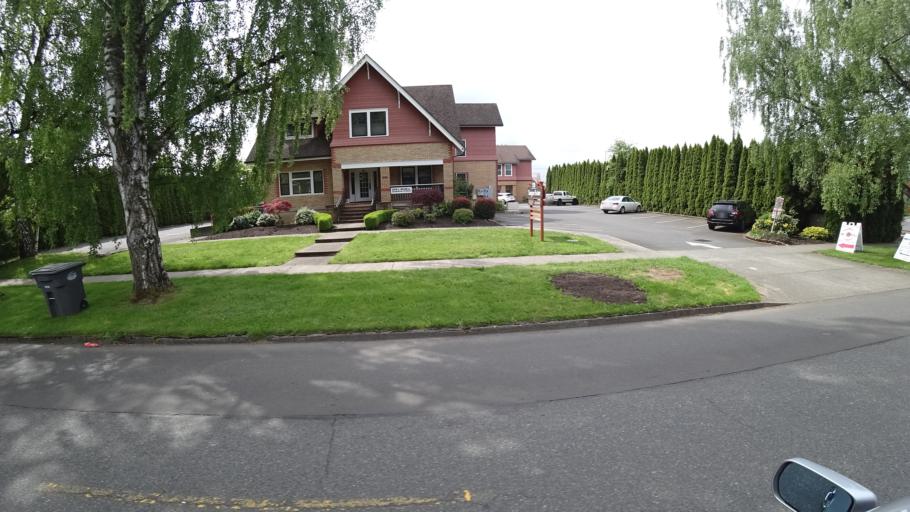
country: US
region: Oregon
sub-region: Washington County
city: Hillsboro
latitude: 45.5227
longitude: -122.9935
